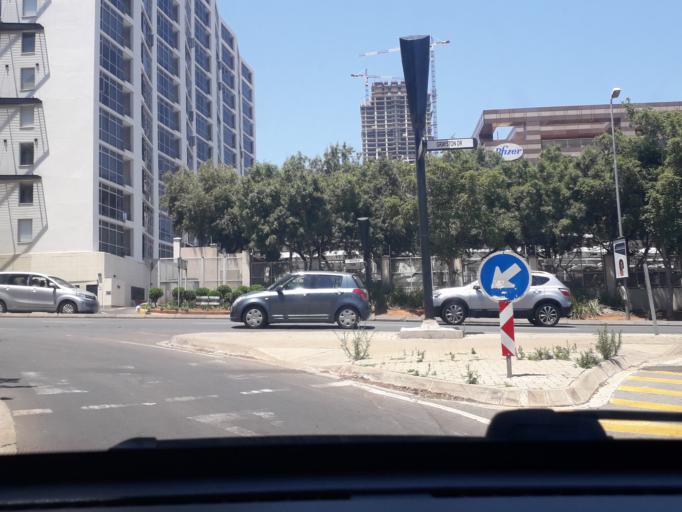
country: ZA
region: Gauteng
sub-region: City of Johannesburg Metropolitan Municipality
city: Johannesburg
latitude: -26.0994
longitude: 28.0534
